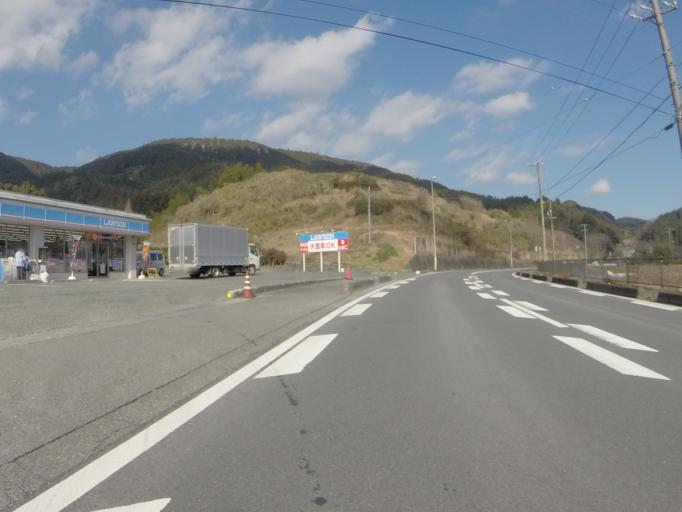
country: JP
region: Shizuoka
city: Fujinomiya
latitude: 35.1625
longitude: 138.5179
